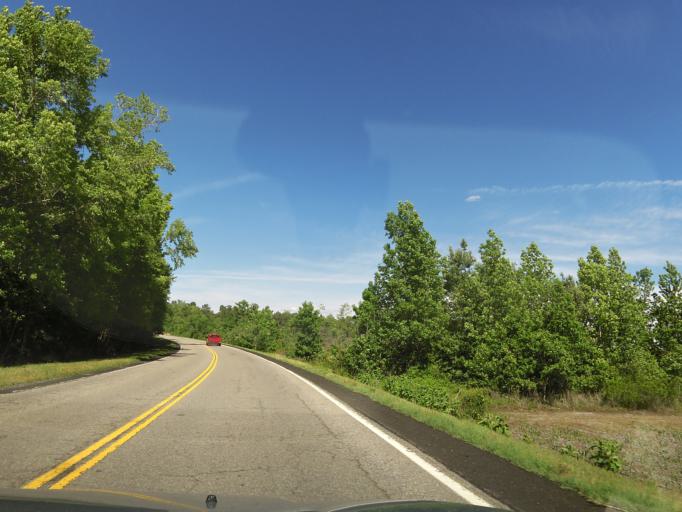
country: US
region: South Carolina
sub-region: Barnwell County
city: Blackville
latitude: 33.3436
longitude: -81.2390
